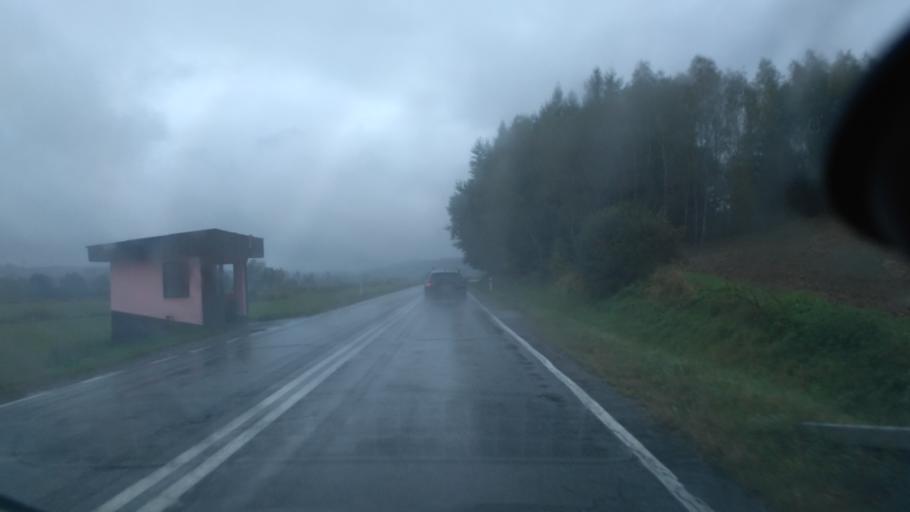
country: PL
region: Subcarpathian Voivodeship
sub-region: Powiat ropczycko-sedziszowski
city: Niedzwiada
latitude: 49.9803
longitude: 21.5595
